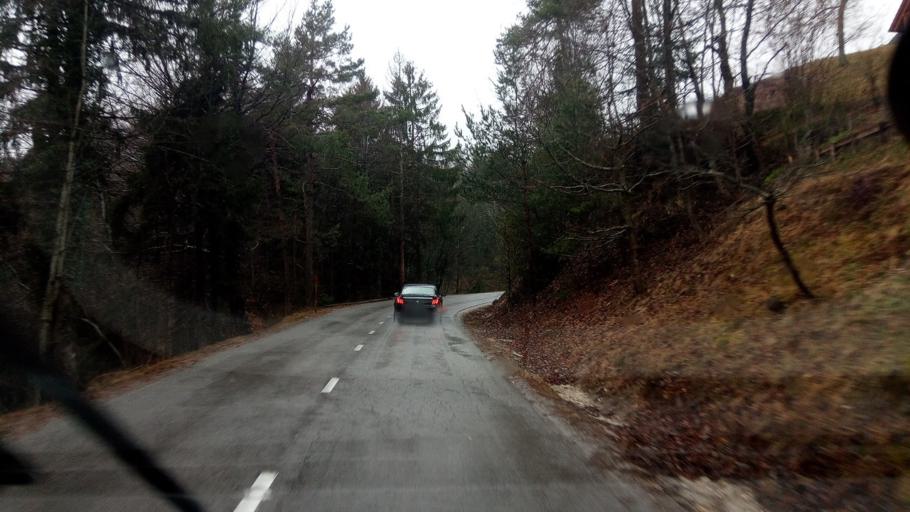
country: SI
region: Horjul
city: Horjul
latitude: 46.0218
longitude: 14.2101
